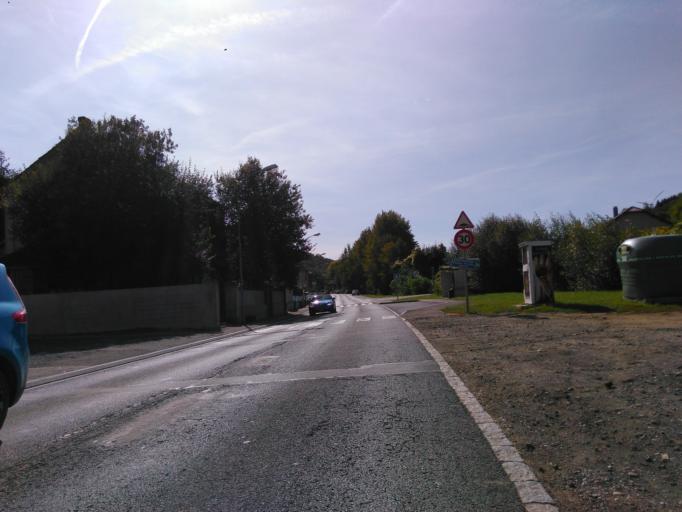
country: FR
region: Lorraine
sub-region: Departement de la Moselle
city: Ottange
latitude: 49.4489
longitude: 6.0250
